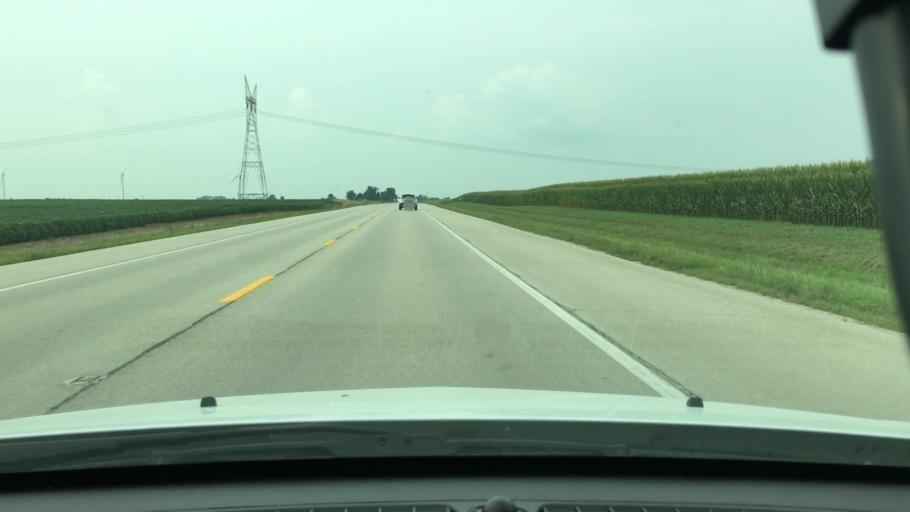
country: US
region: Illinois
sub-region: DeKalb County
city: Waterman
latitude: 41.7997
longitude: -88.7540
